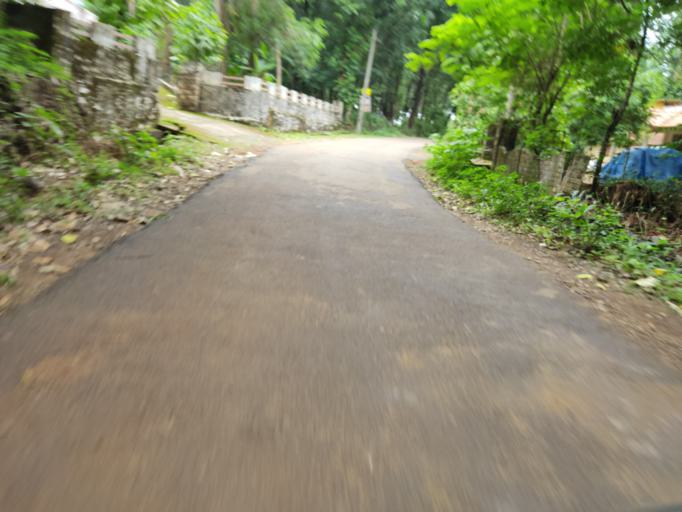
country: IN
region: Kerala
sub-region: Malappuram
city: Manjeri
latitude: 11.2227
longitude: 76.2537
